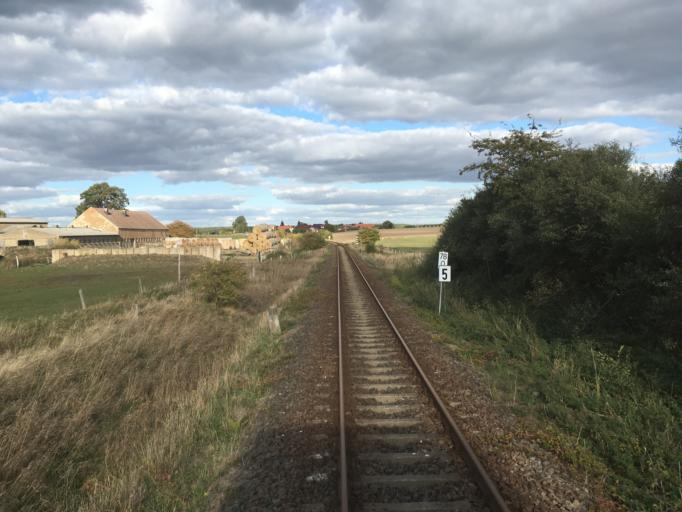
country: DE
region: Mecklenburg-Vorpommern
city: Malchow
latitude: 53.5172
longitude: 12.4449
